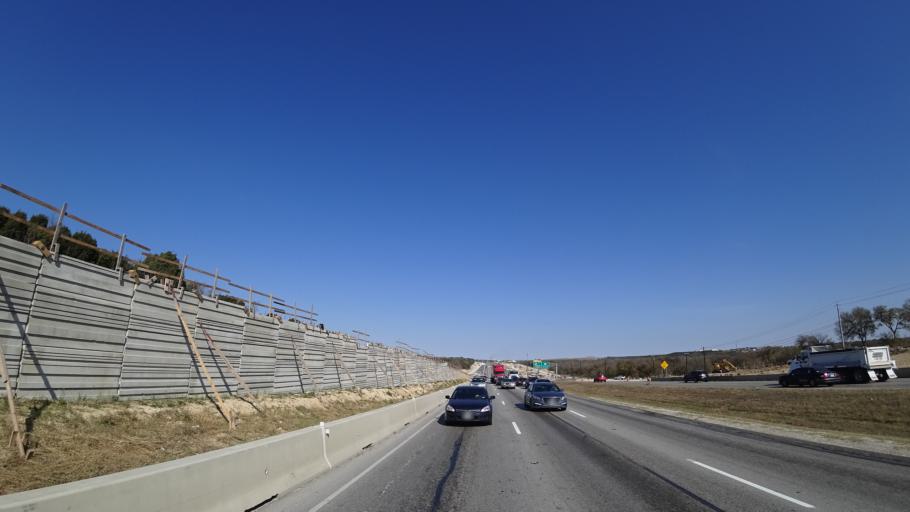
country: US
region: Texas
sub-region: Travis County
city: Austin
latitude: 30.2934
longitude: -97.6635
